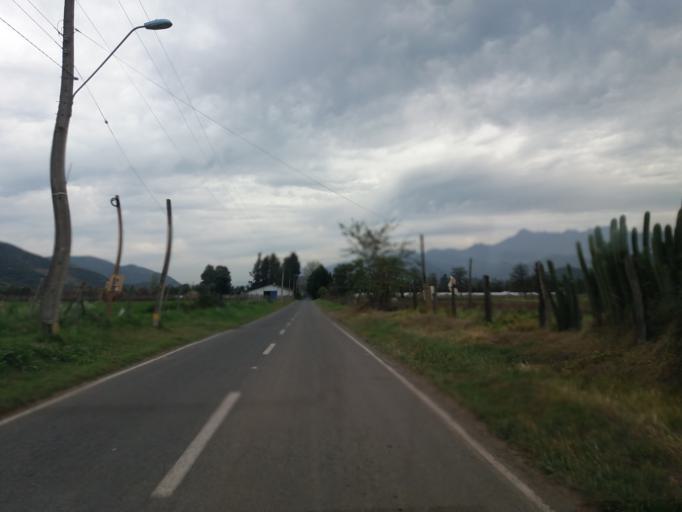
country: CL
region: Valparaiso
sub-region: Provincia de Quillota
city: Quillota
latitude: -32.8893
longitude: -71.1081
